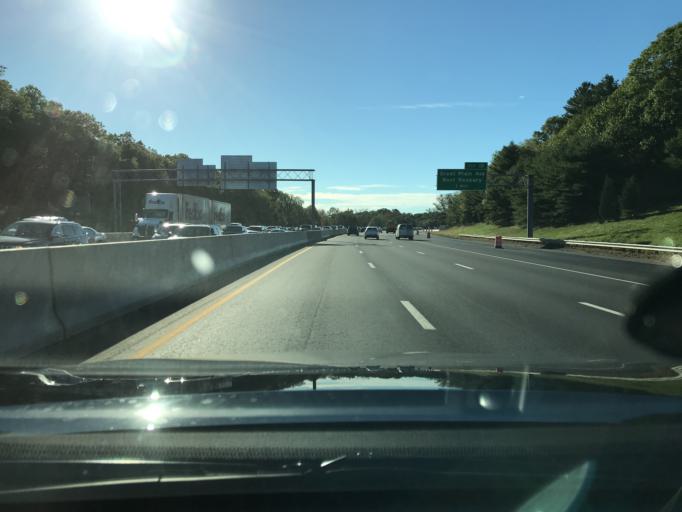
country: US
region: Massachusetts
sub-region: Norfolk County
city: Needham
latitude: 42.2831
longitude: -71.2034
